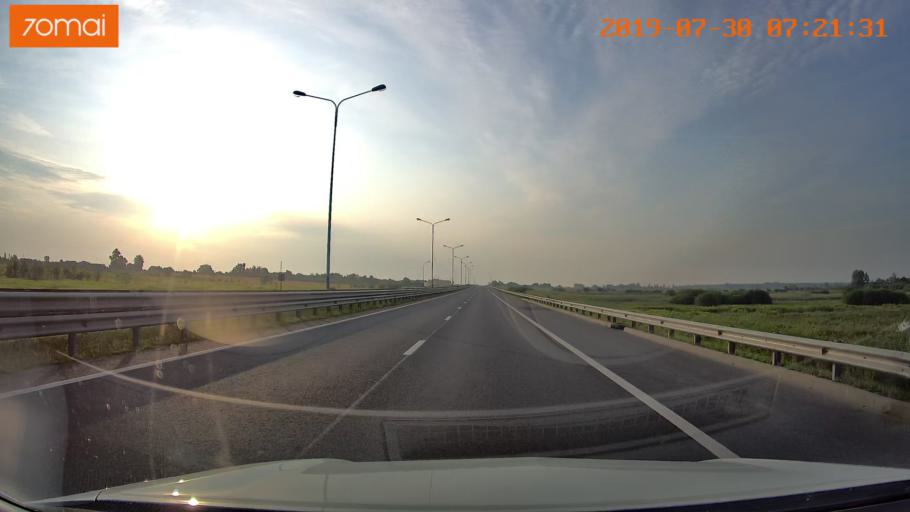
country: RU
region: Kaliningrad
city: Bol'shoe Isakovo
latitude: 54.6960
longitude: 20.7311
